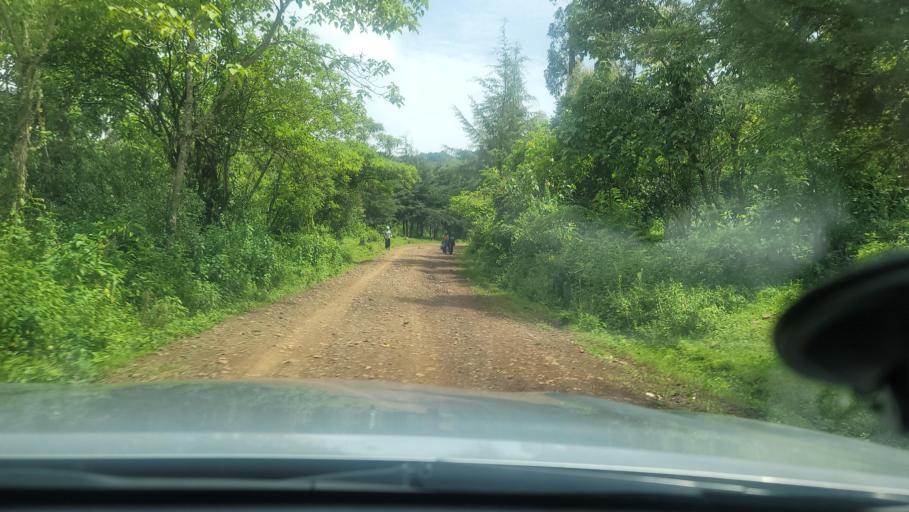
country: ET
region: Oromiya
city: Agaro
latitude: 7.8094
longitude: 36.4118
